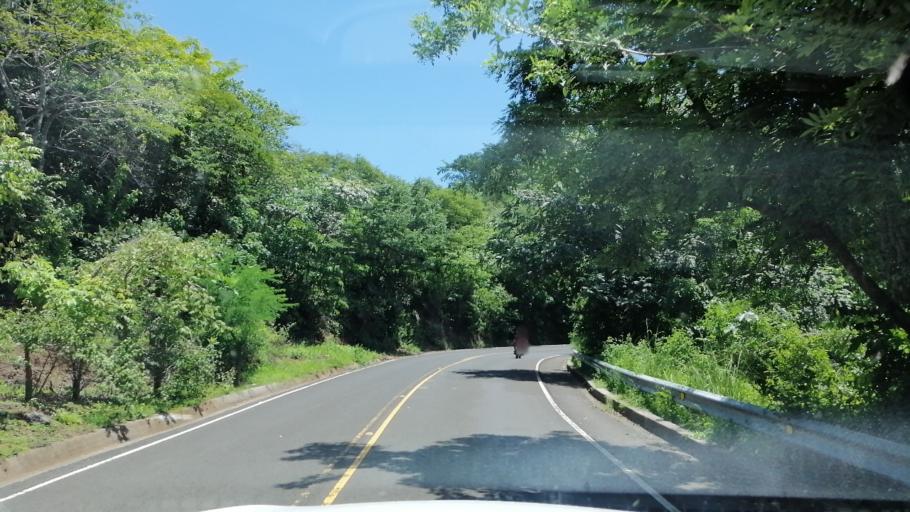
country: SV
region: San Miguel
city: Ciudad Barrios
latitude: 13.7913
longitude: -88.2879
